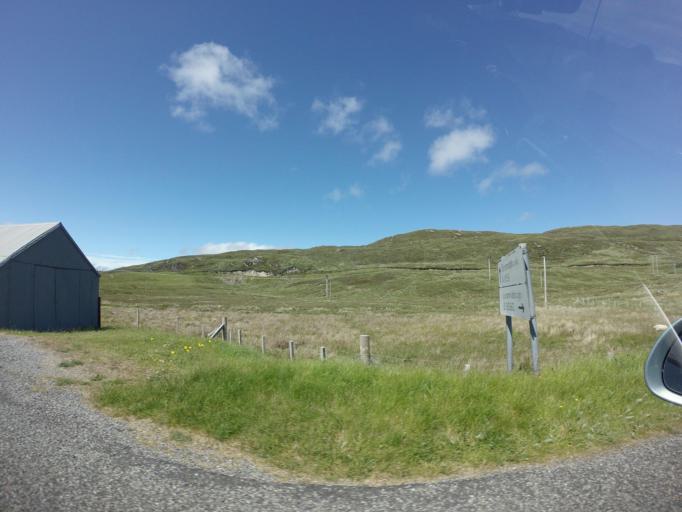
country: GB
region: Scotland
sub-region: Eilean Siar
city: Harris
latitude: 58.0865
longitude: -6.6373
